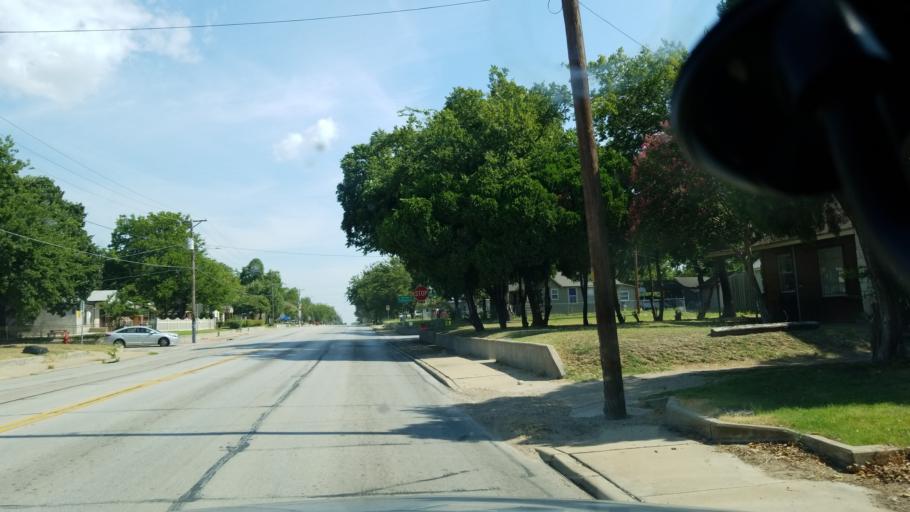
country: US
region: Texas
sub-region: Dallas County
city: Grand Prairie
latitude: 32.7525
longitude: -96.9602
